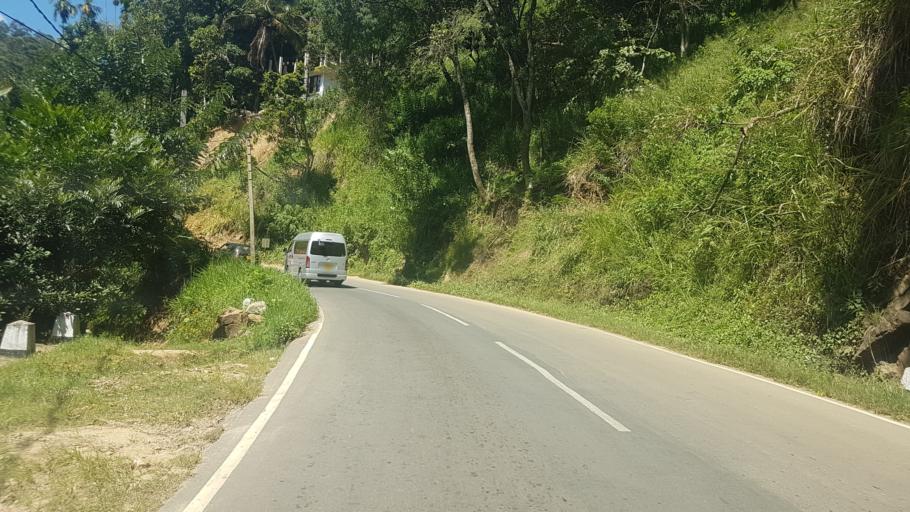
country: LK
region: Uva
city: Badulla
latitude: 6.8696
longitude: 81.0499
